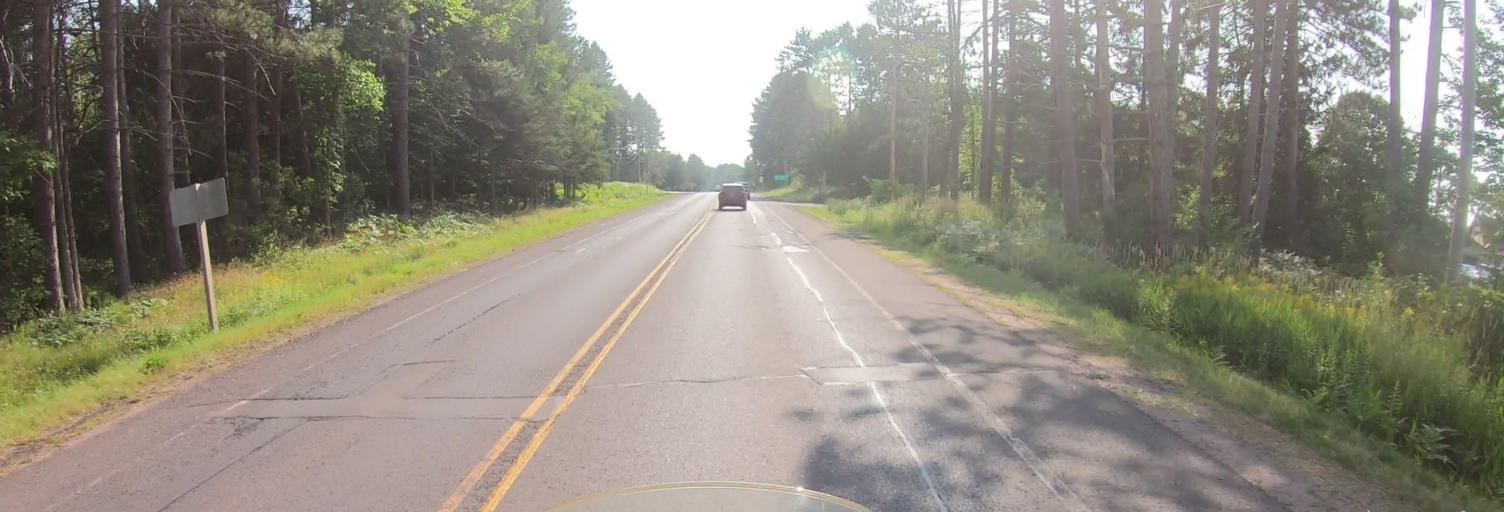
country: US
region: Wisconsin
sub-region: Iron County
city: Hurley
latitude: 46.4472
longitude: -90.1924
